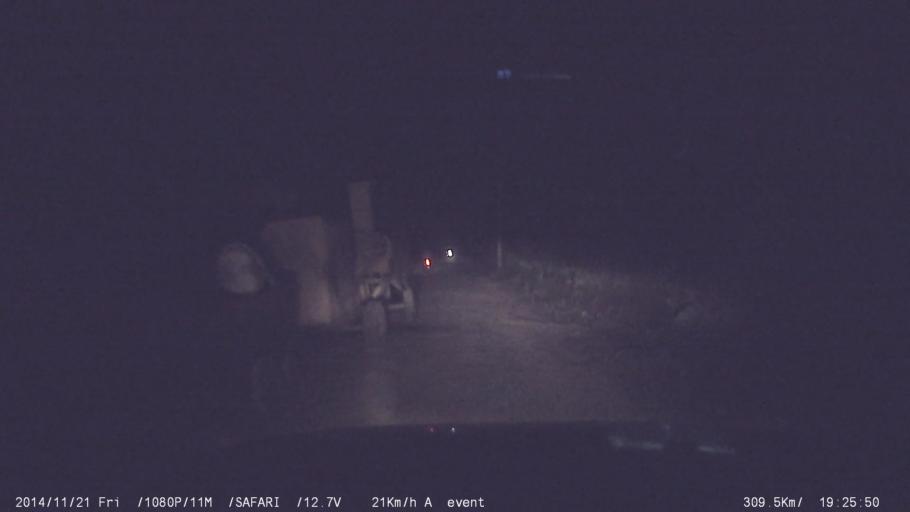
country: IN
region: Tamil Nadu
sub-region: Kancheepuram
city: Singapperumalkovil
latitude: 12.7986
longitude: 79.9845
